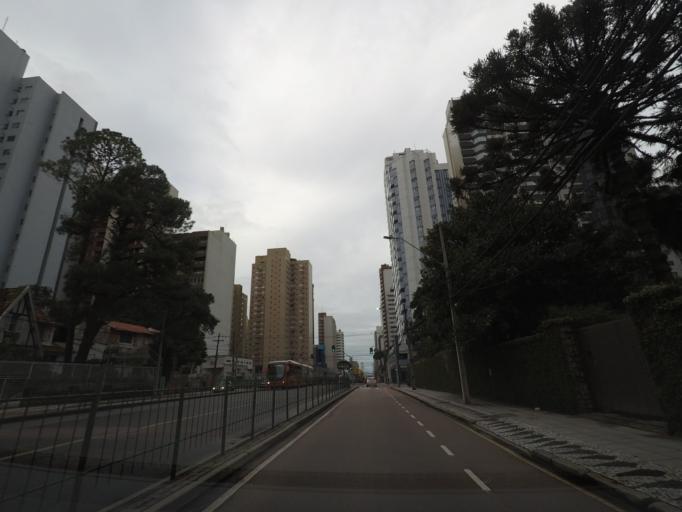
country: BR
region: Parana
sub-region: Curitiba
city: Curitiba
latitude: -25.4435
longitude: -49.2816
